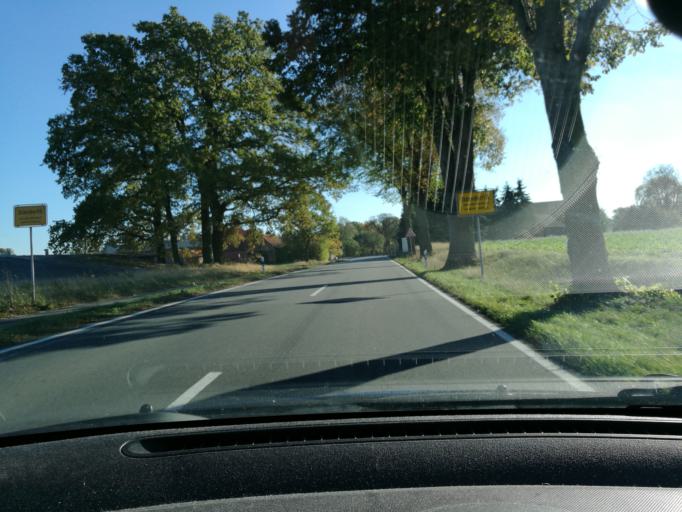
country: DE
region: Lower Saxony
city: Nahrendorf
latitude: 53.1599
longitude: 10.8075
